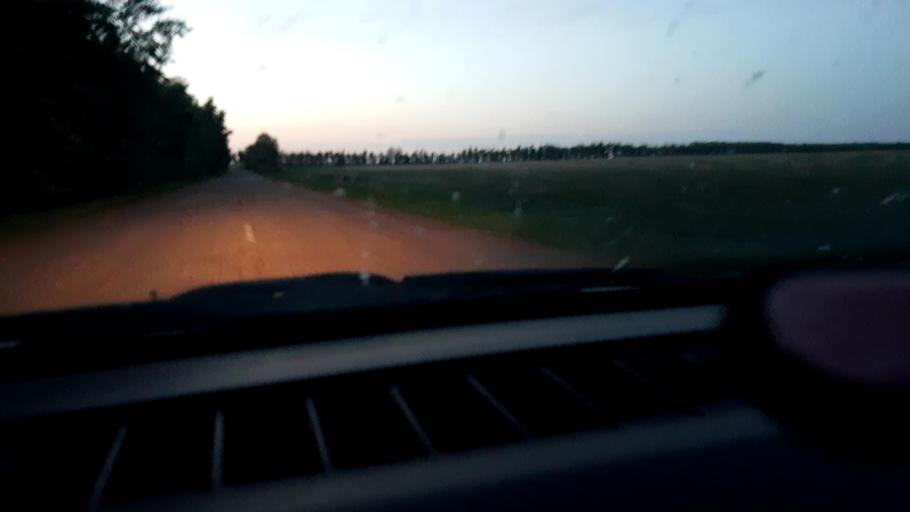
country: RU
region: Bashkortostan
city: Asanovo
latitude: 54.8247
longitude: 55.5967
